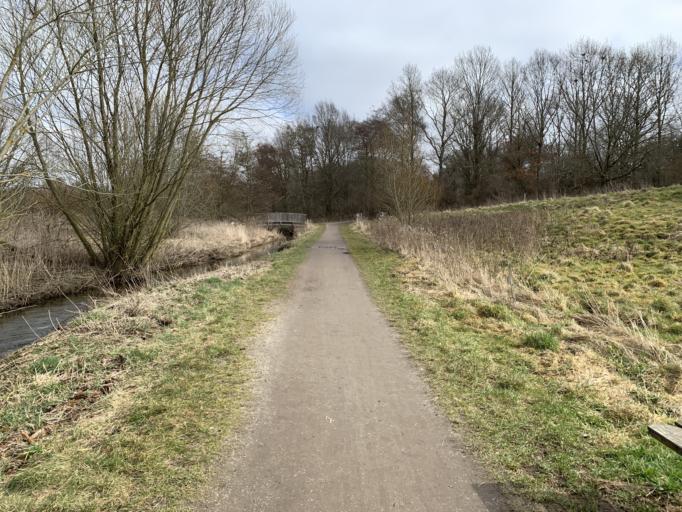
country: DK
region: South Denmark
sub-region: Odense Kommune
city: Odense
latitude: 55.4185
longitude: 10.3197
